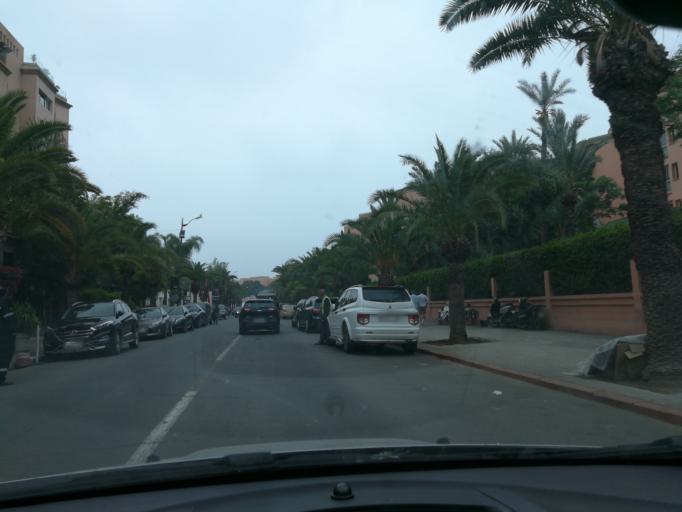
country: MA
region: Marrakech-Tensift-Al Haouz
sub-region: Marrakech
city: Marrakesh
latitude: 31.6221
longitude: -8.0018
